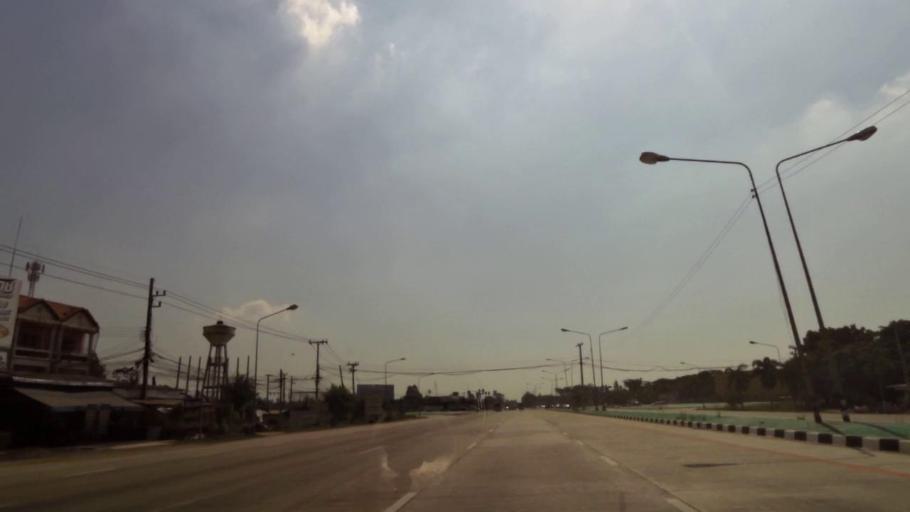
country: TH
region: Phichit
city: Bueng Na Rang
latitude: 16.1253
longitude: 100.1256
